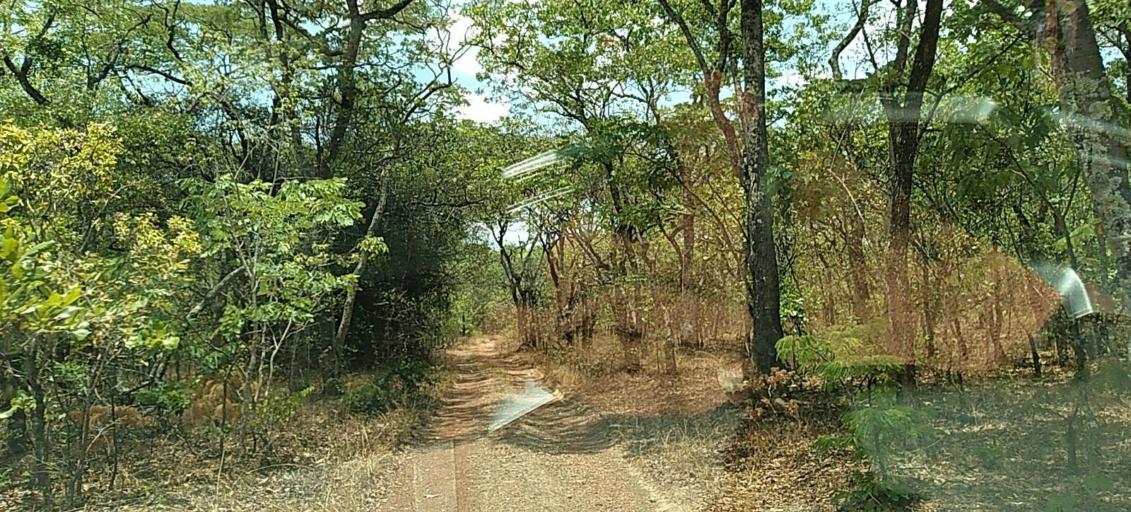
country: ZM
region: Copperbelt
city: Chililabombwe
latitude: -12.4569
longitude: 27.6982
